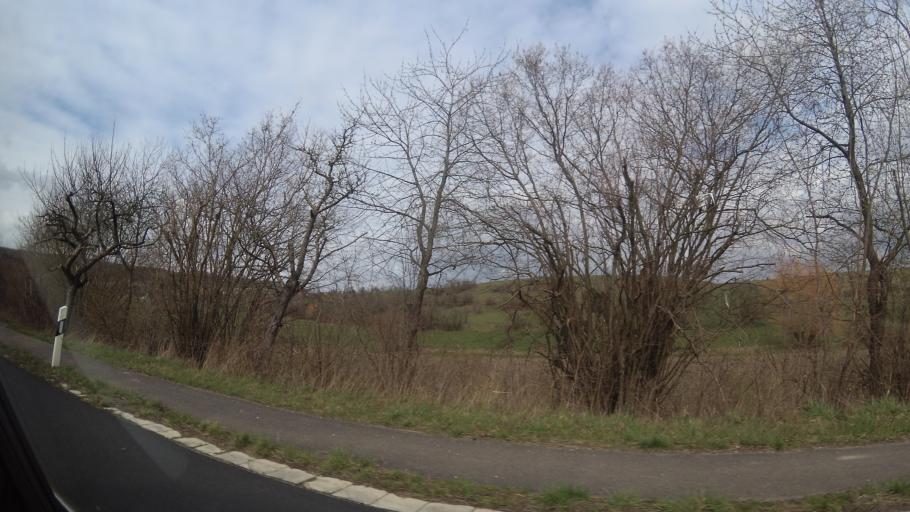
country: DE
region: Saarland
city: Gersheim
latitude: 49.1856
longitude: 7.2281
